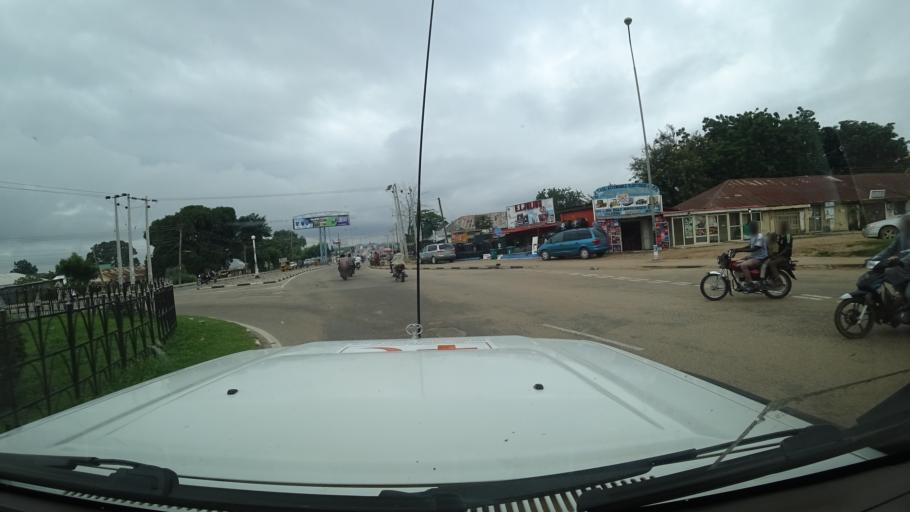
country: NG
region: Niger
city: Minna
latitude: 9.6109
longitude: 6.5512
